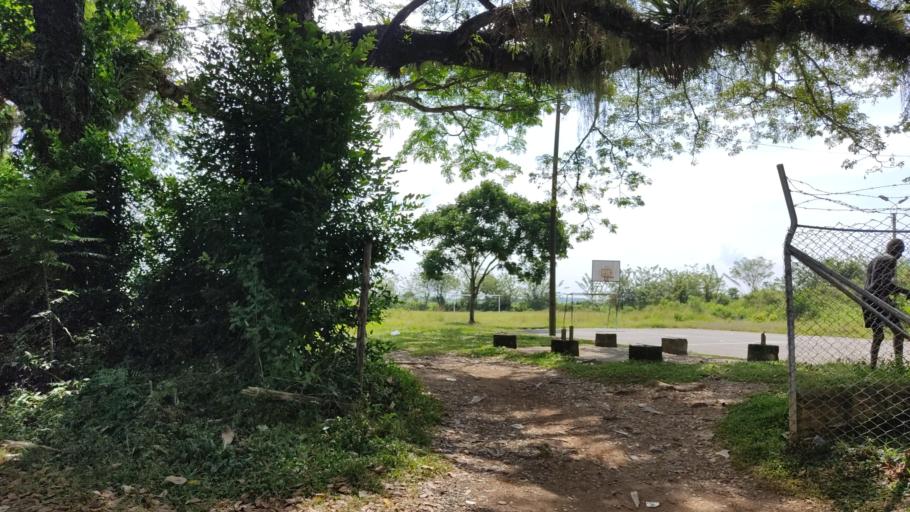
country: CO
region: Cauca
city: Buenos Aires
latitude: 3.1298
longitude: -76.5918
